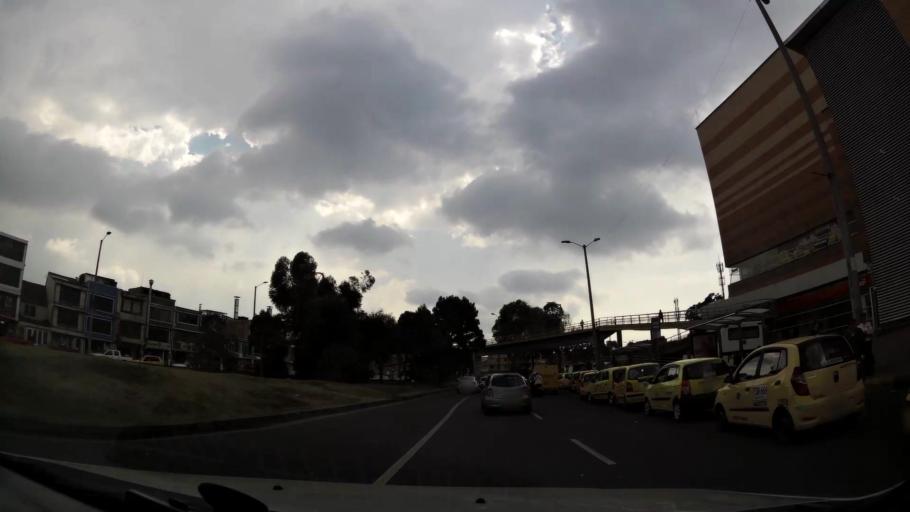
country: CO
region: Bogota D.C.
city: Bogota
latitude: 4.5900
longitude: -74.1240
